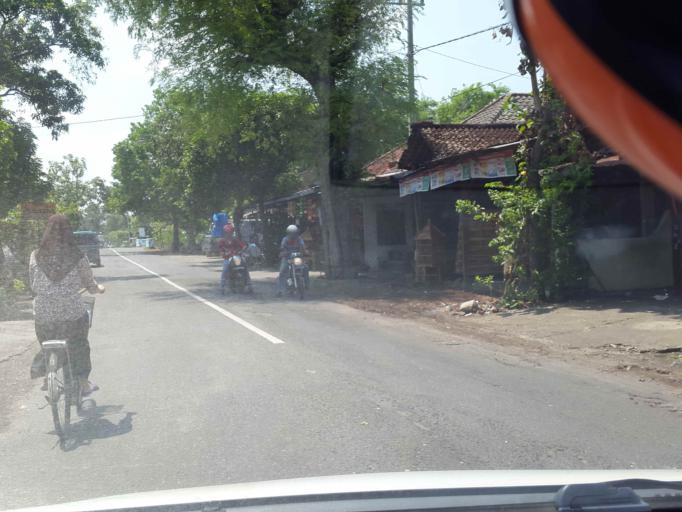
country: ID
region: East Java
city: Ponorogo
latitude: -7.8490
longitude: 111.4692
